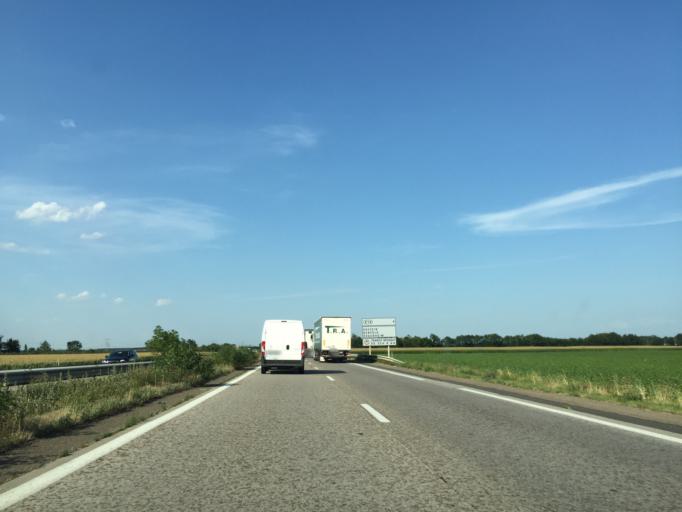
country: FR
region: Alsace
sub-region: Departement du Bas-Rhin
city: Selestat
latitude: 48.2920
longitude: 7.4644
